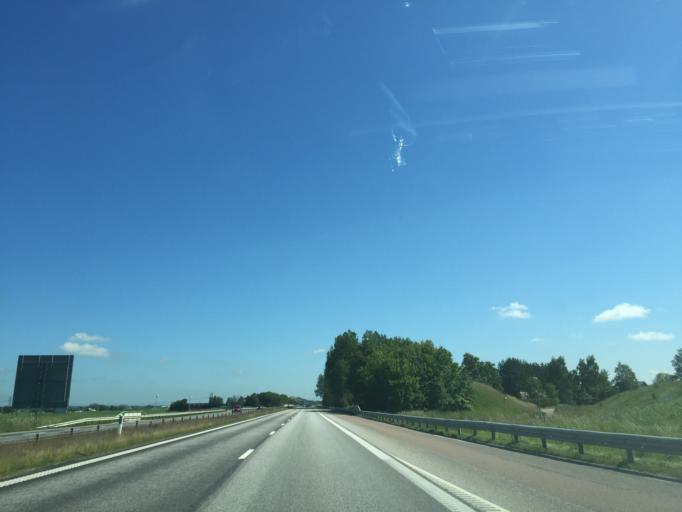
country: SE
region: Skane
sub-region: Helsingborg
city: Hyllinge
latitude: 56.1047
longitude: 12.8572
